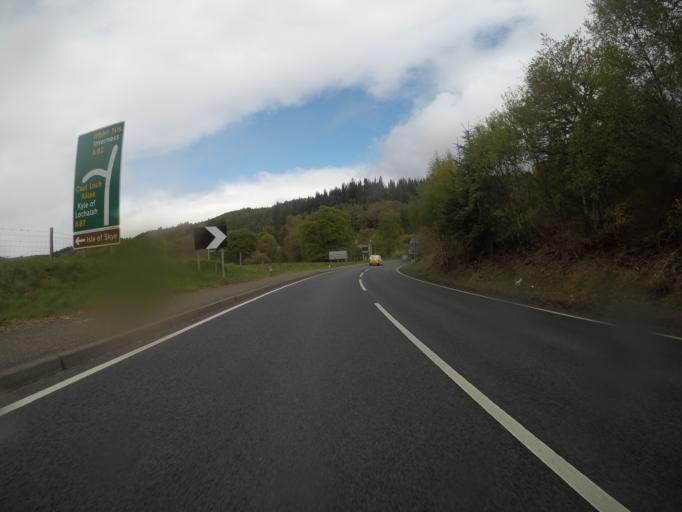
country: GB
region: Scotland
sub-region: Highland
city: Spean Bridge
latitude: 57.0679
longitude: -4.7924
